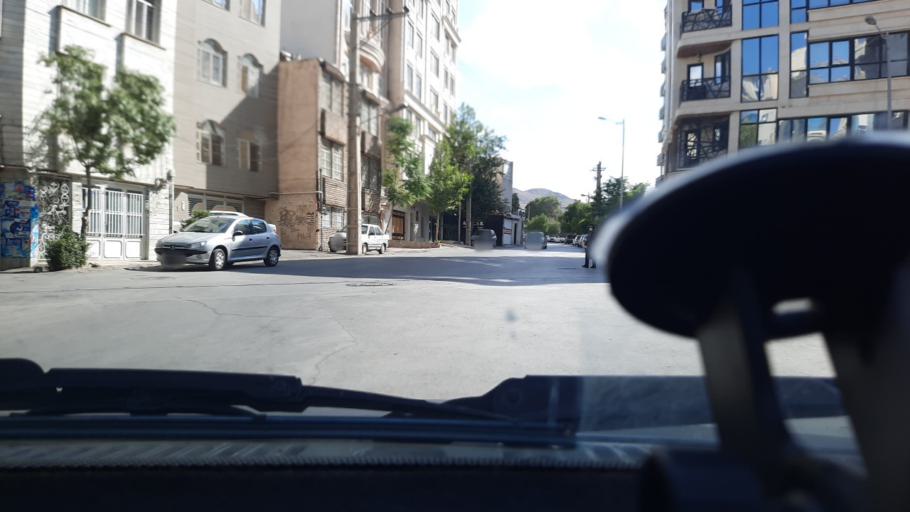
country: IR
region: Markazi
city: Arak
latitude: 34.0785
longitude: 49.6875
